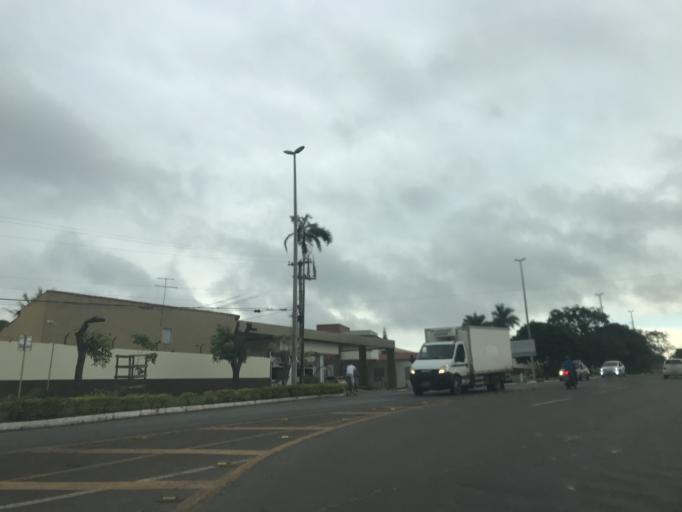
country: BR
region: Federal District
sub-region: Brasilia
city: Brasilia
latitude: -15.6828
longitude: -47.8370
